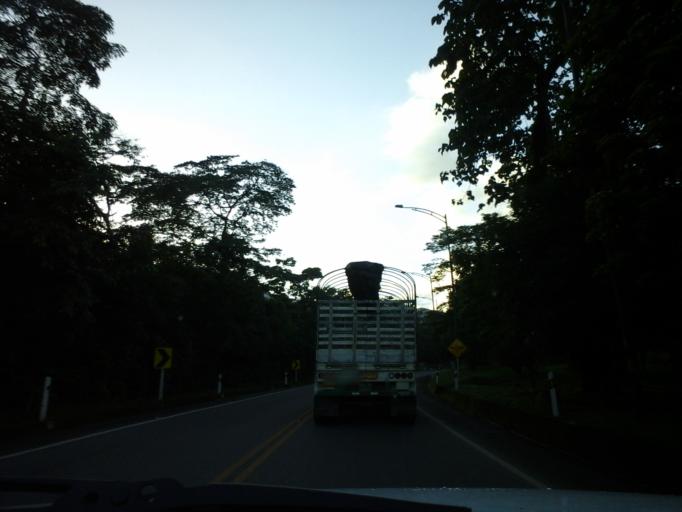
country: CO
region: Meta
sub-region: Villavicencio
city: Villavicencio
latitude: 4.1280
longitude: -73.6531
